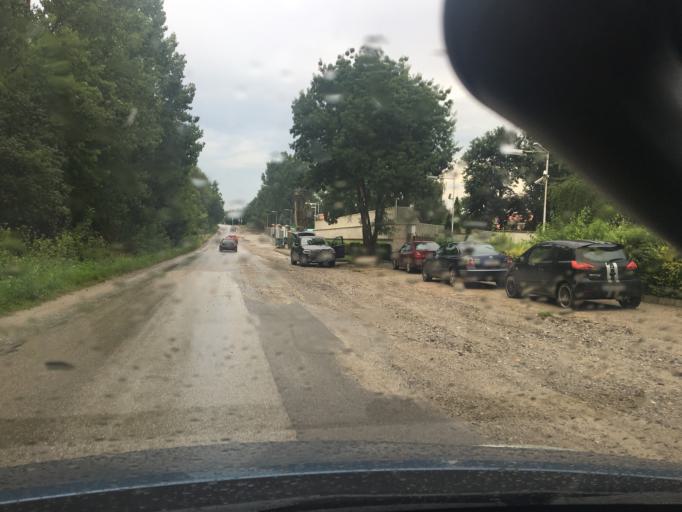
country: BG
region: Sofia-Capital
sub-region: Stolichna Obshtina
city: Sofia
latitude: 42.6392
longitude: 23.2958
